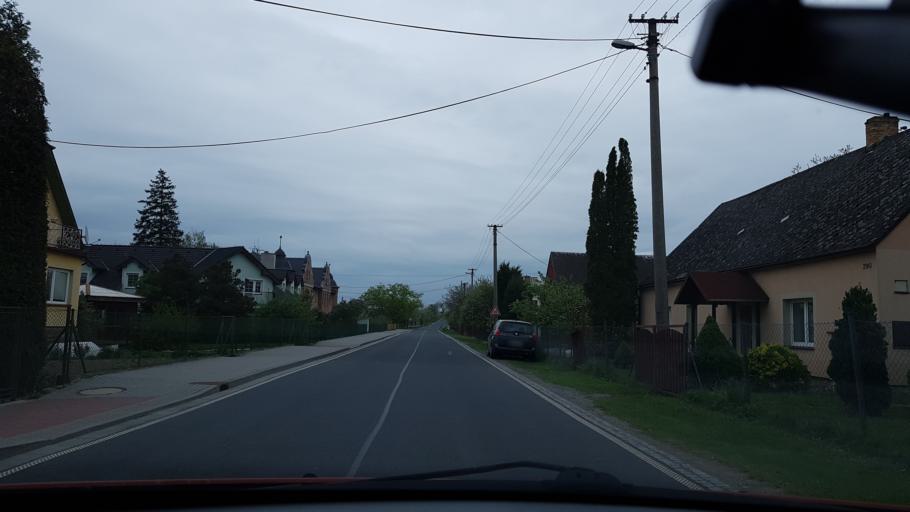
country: CZ
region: Olomoucky
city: Javornik
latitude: 50.3887
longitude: 17.0809
